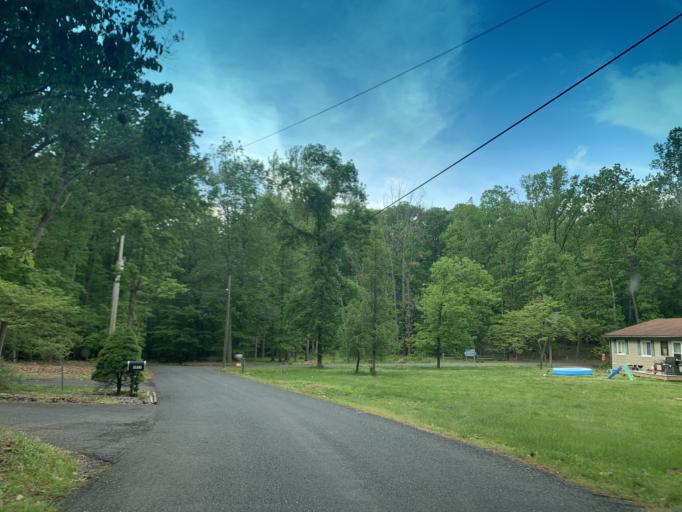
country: US
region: Pennsylvania
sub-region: York County
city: Susquehanna Trails
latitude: 39.6796
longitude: -76.2610
